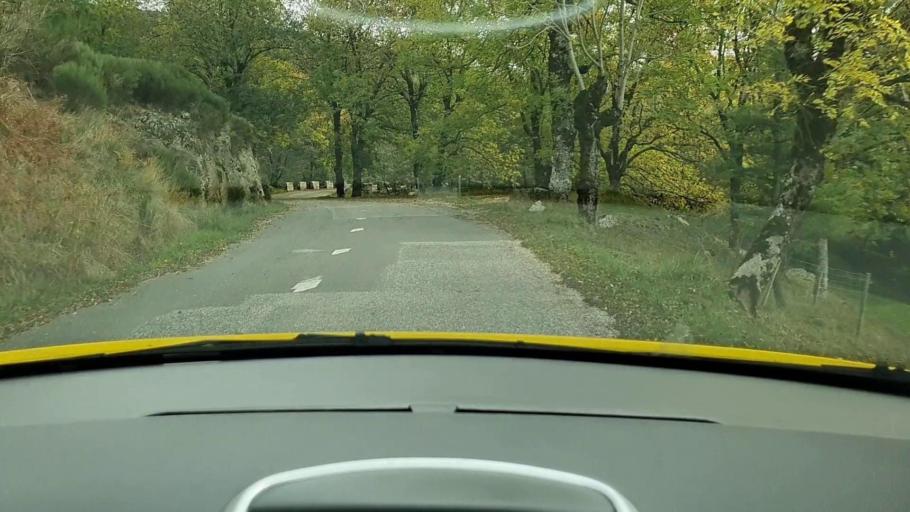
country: FR
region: Languedoc-Roussillon
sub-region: Departement de la Lozere
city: Meyrueis
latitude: 44.0763
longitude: 3.4915
